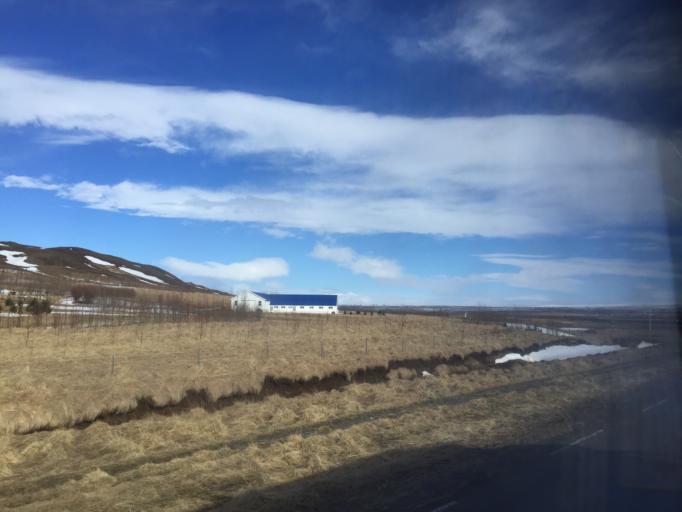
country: IS
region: South
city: Selfoss
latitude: 64.2726
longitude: -20.3645
